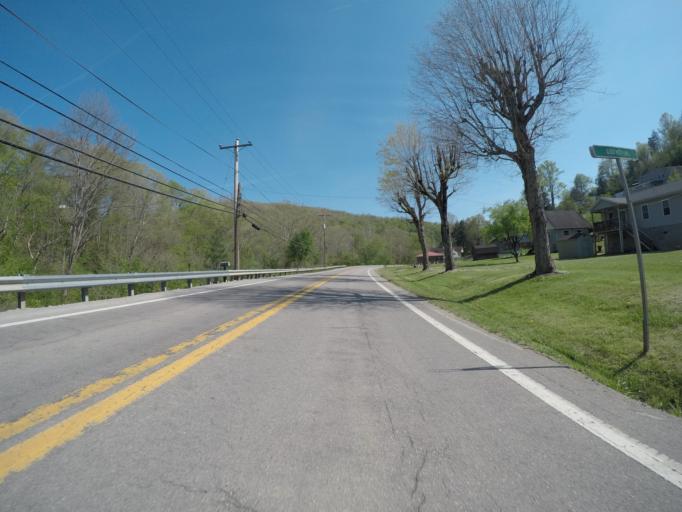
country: US
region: West Virginia
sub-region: Kanawha County
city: Clendenin
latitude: 38.5020
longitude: -81.3489
